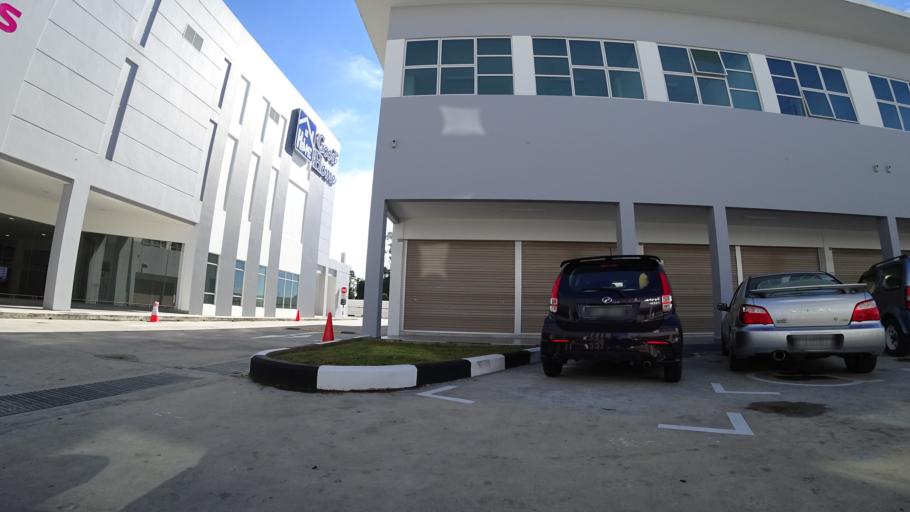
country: BN
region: Brunei and Muara
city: Bandar Seri Begawan
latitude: 4.9485
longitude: 114.9672
